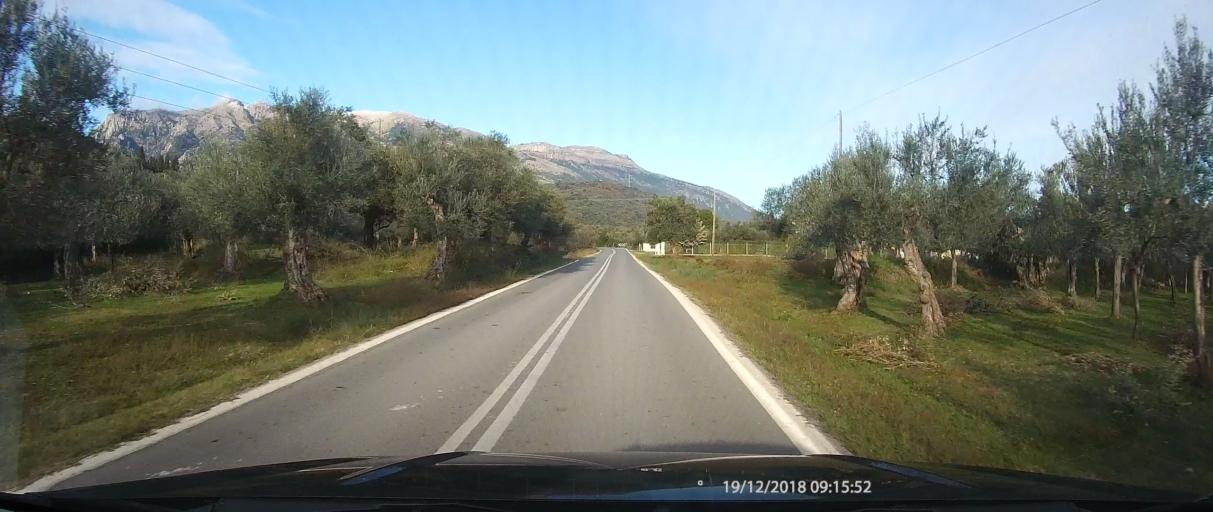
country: GR
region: Peloponnese
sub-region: Nomos Lakonias
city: Magoula
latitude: 37.0923
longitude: 22.3720
